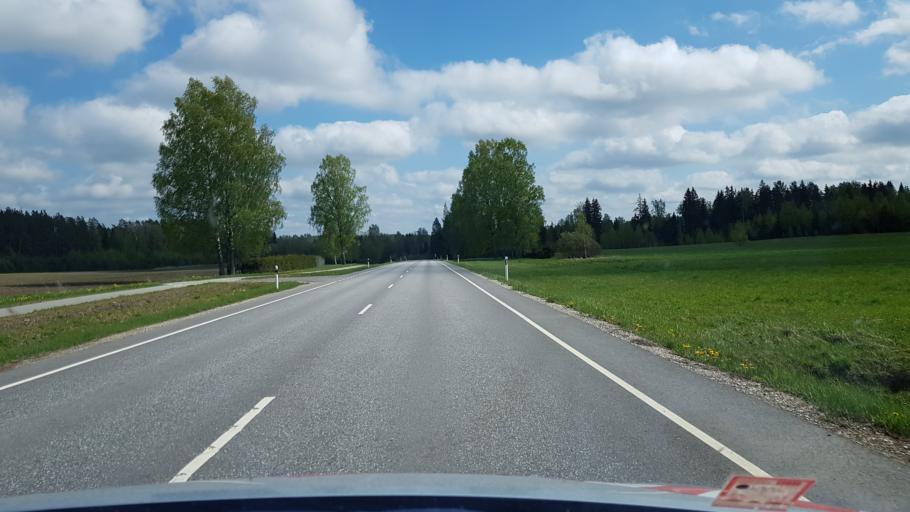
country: EE
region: Viljandimaa
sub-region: Karksi vald
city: Karksi-Nuia
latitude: 58.0870
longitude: 25.5848
